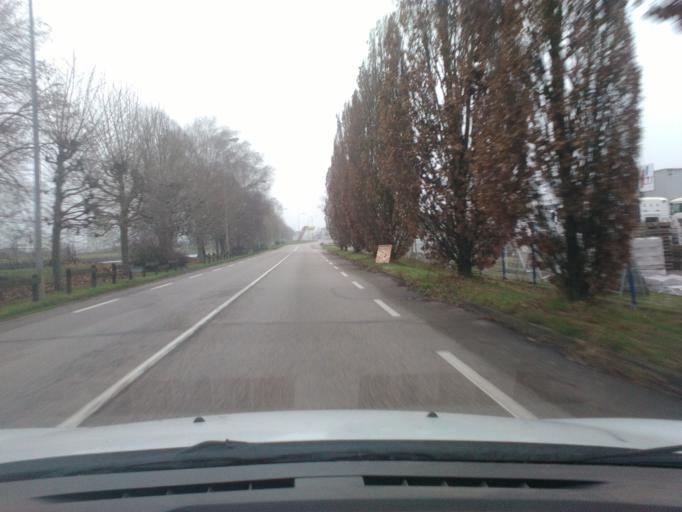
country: FR
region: Lorraine
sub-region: Departement des Vosges
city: Chavelot
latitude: 48.2186
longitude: 6.4375
